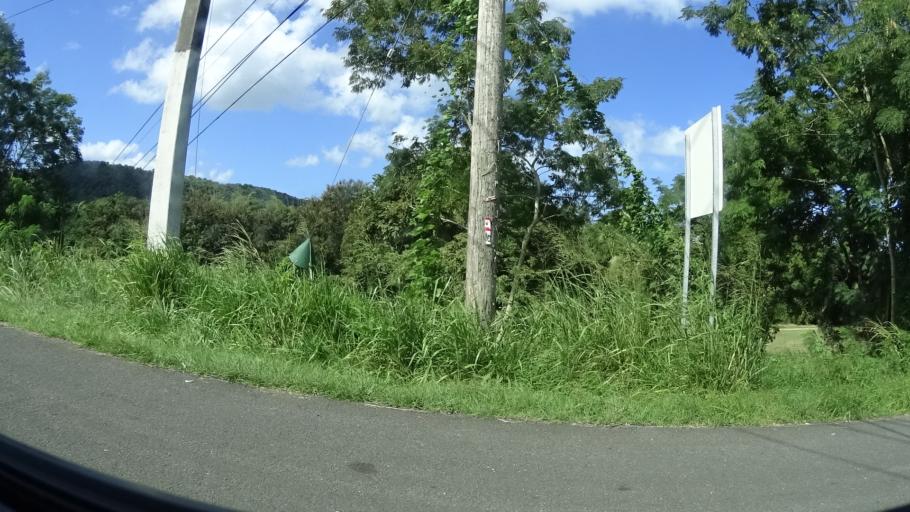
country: PR
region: Rio Grande
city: Palmer
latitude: 18.3733
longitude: -65.7615
